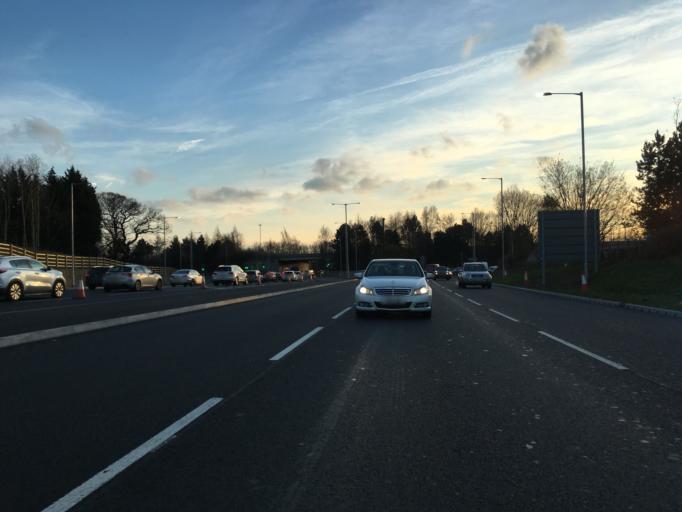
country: GB
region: England
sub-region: Borough of Stockport
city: Cheadle Hulme
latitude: 53.3575
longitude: -2.1996
